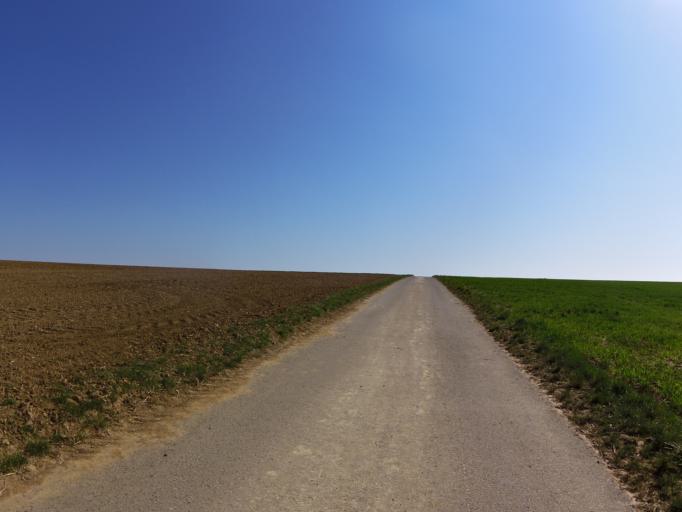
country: DE
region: Bavaria
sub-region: Regierungsbezirk Unterfranken
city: Biebelried
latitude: 49.8105
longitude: 10.0790
